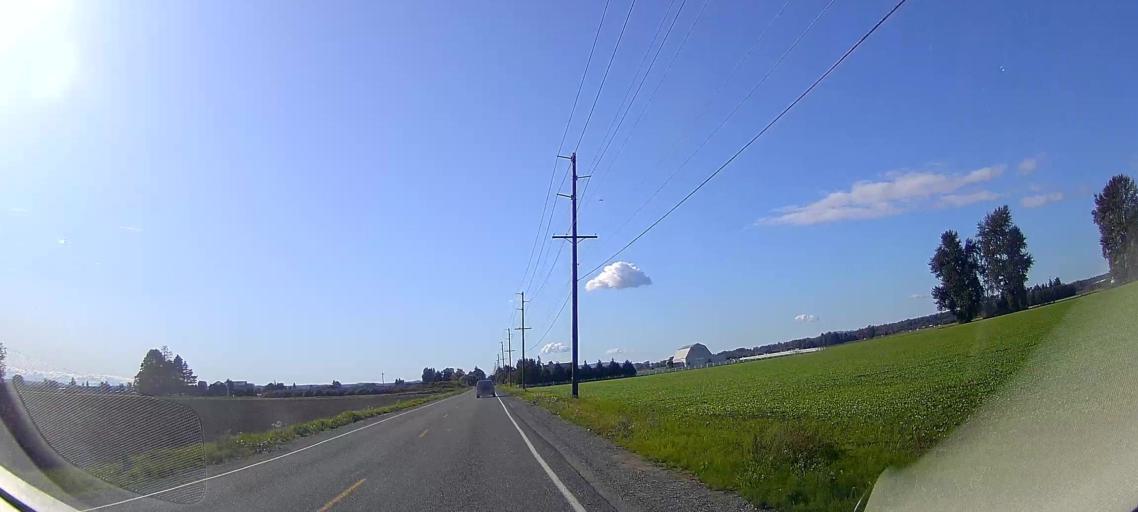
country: US
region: Washington
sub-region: Skagit County
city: Mount Vernon
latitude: 48.4427
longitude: -122.3852
